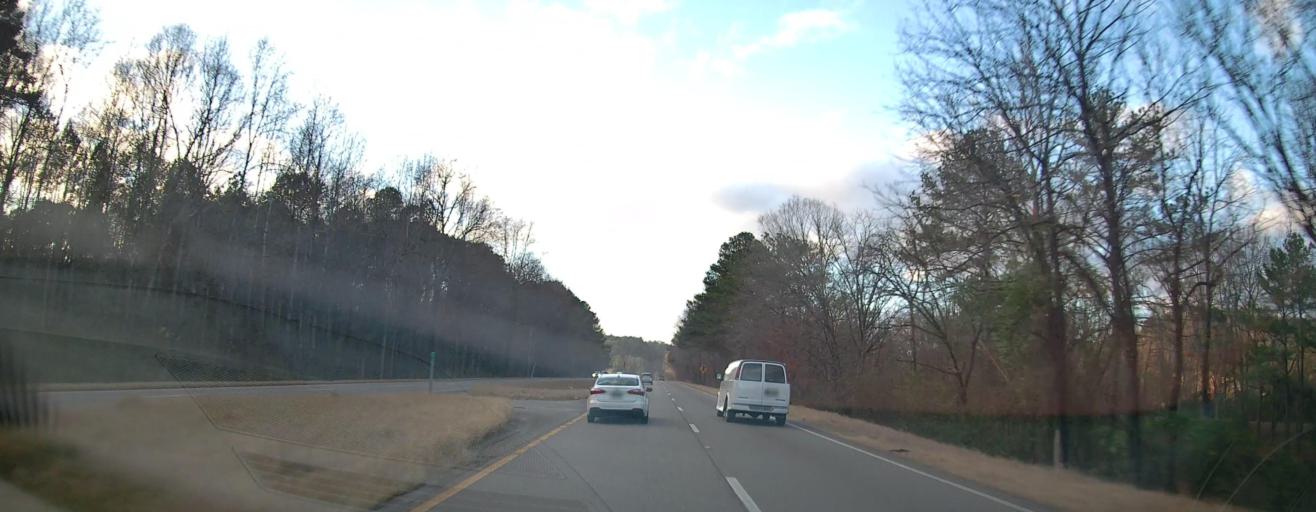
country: US
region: Alabama
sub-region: Etowah County
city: Glencoe
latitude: 33.9437
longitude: -85.9203
